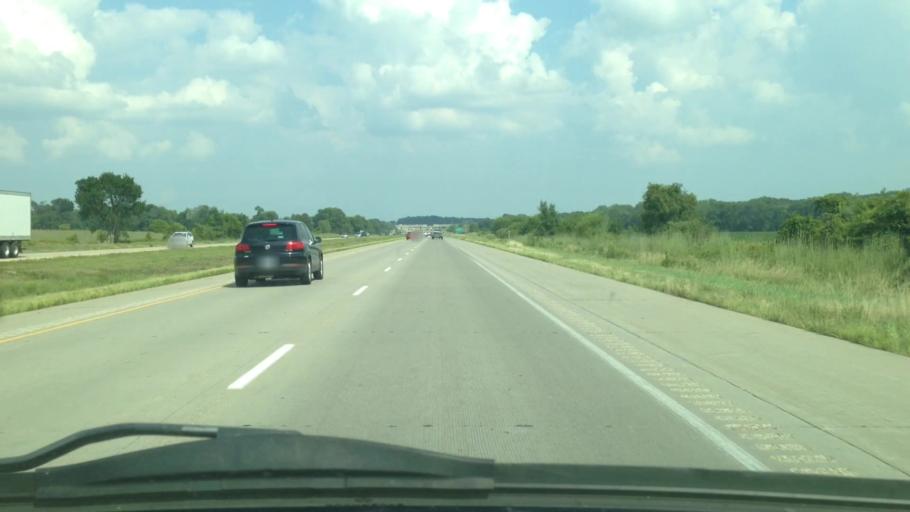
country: US
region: Iowa
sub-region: Black Hawk County
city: Elk Run Heights
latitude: 42.4511
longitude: -92.2367
